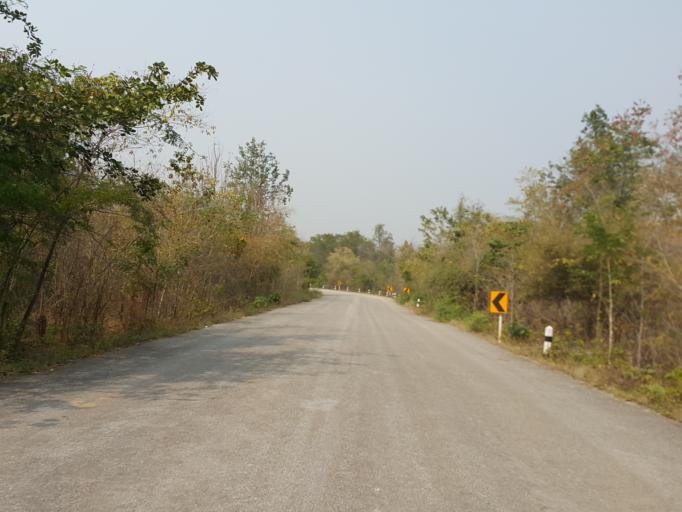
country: TH
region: Lampang
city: Mae Phrik
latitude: 17.5022
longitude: 99.0832
